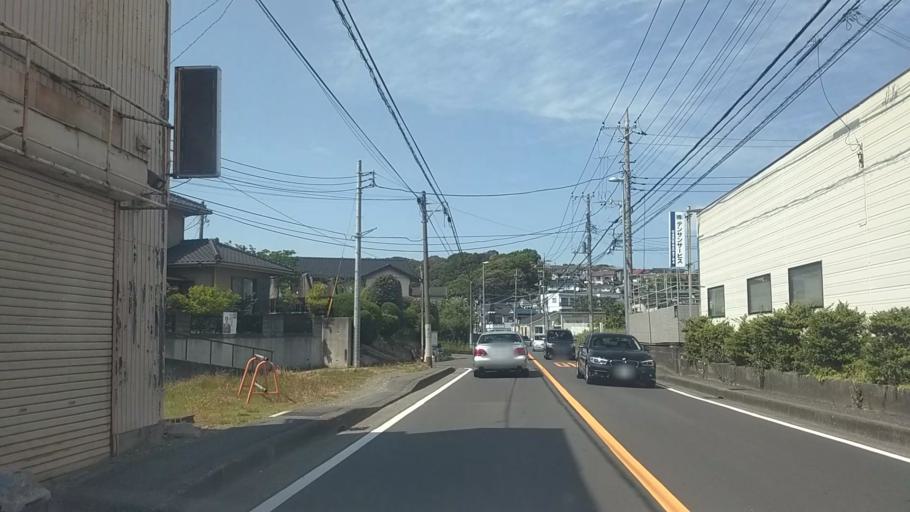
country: JP
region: Kanagawa
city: Kamakura
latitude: 35.3556
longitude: 139.5800
